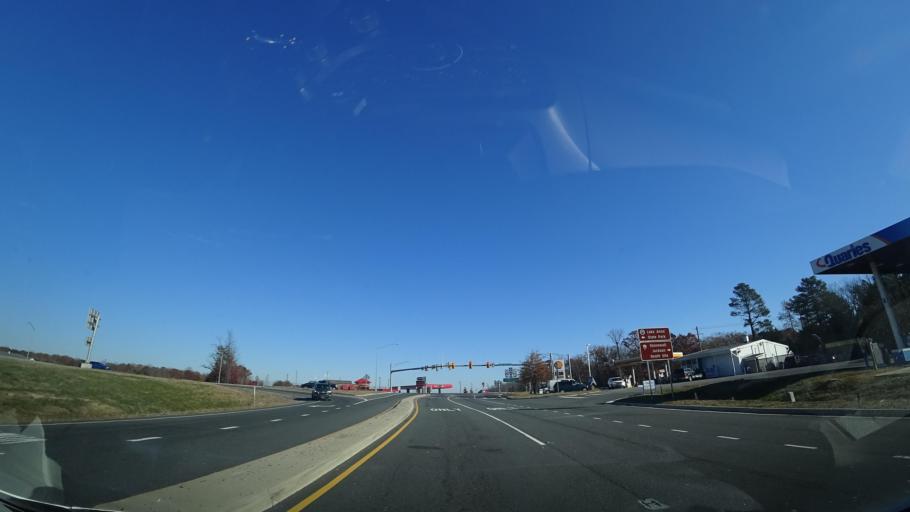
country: US
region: Virginia
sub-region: Spotsylvania County
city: Spotsylvania Courthouse
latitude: 38.1314
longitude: -77.5099
